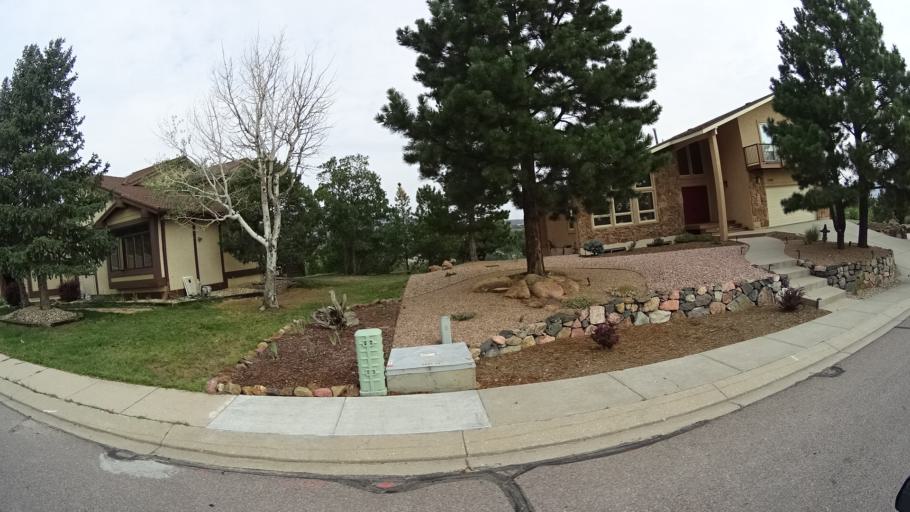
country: US
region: Colorado
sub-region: El Paso County
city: Air Force Academy
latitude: 38.9388
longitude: -104.8557
